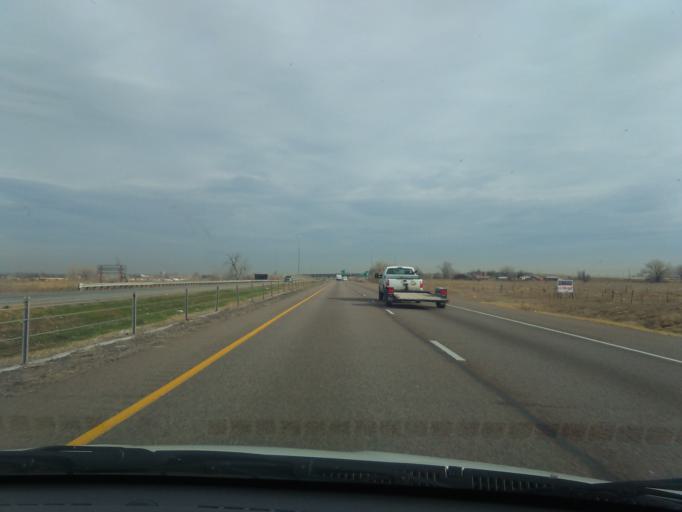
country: US
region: Colorado
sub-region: Adams County
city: Brighton
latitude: 39.9029
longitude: -104.8358
